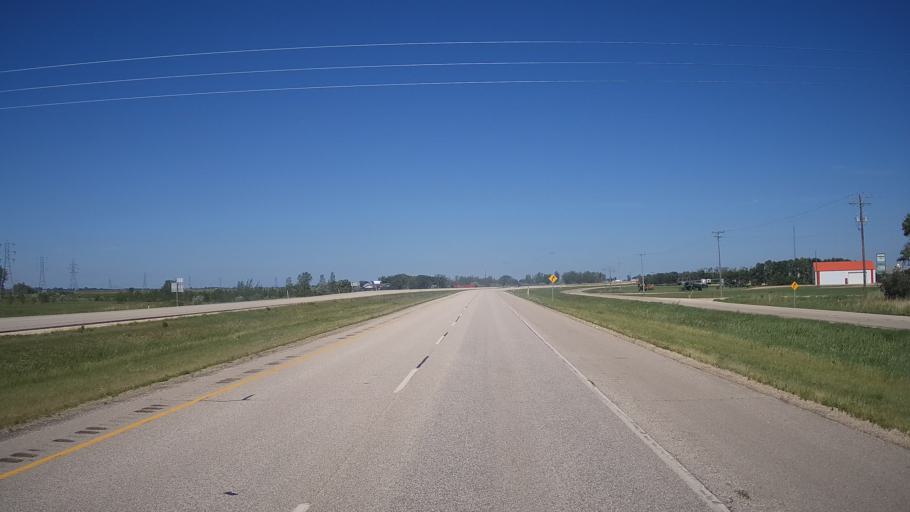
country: CA
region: Manitoba
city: Portage la Prairie
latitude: 49.9608
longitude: -98.3468
